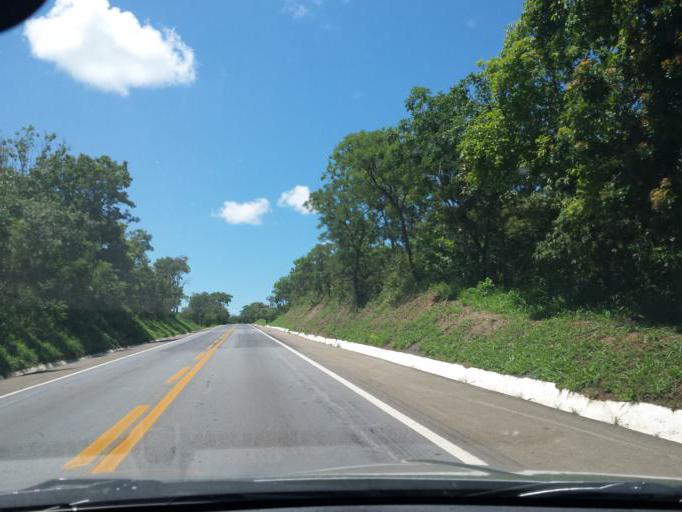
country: BR
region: Goias
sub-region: Luziania
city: Luziania
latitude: -16.4156
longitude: -47.8243
